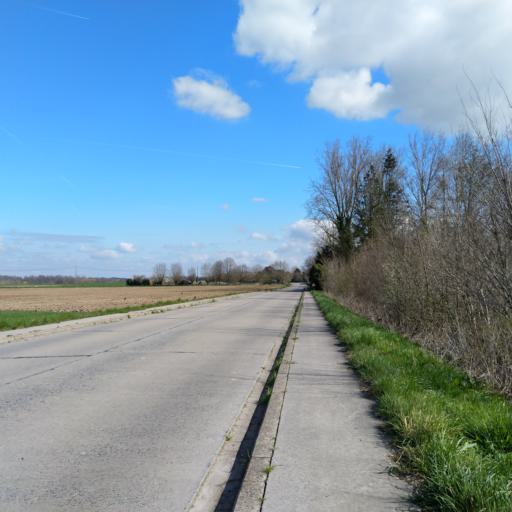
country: BE
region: Wallonia
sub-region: Province du Hainaut
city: Lens
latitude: 50.5801
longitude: 3.9282
